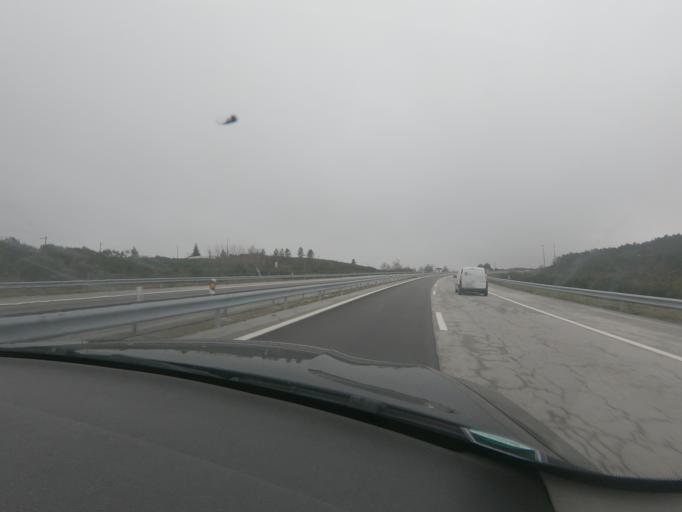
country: PT
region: Viseu
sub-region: Castro Daire
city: Castro Daire
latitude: 40.9523
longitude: -7.8927
